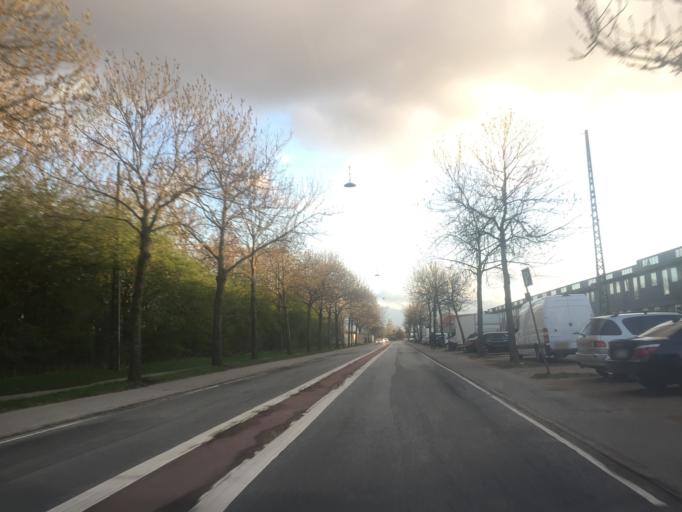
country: DK
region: Capital Region
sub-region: Hvidovre Kommune
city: Hvidovre
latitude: 55.6579
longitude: 12.4891
